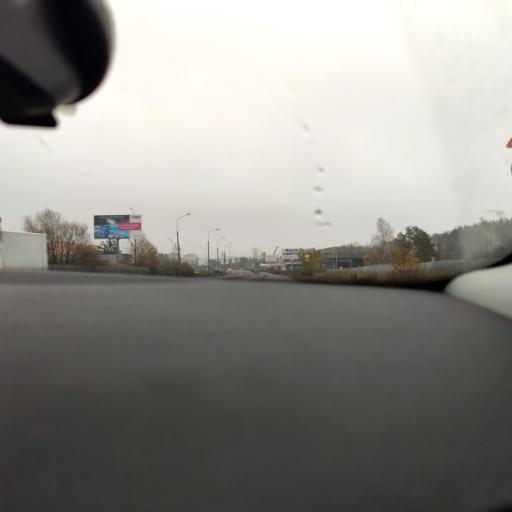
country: RU
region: Moskovskaya
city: Pavlovskaya Sloboda
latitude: 55.8119
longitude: 37.1161
